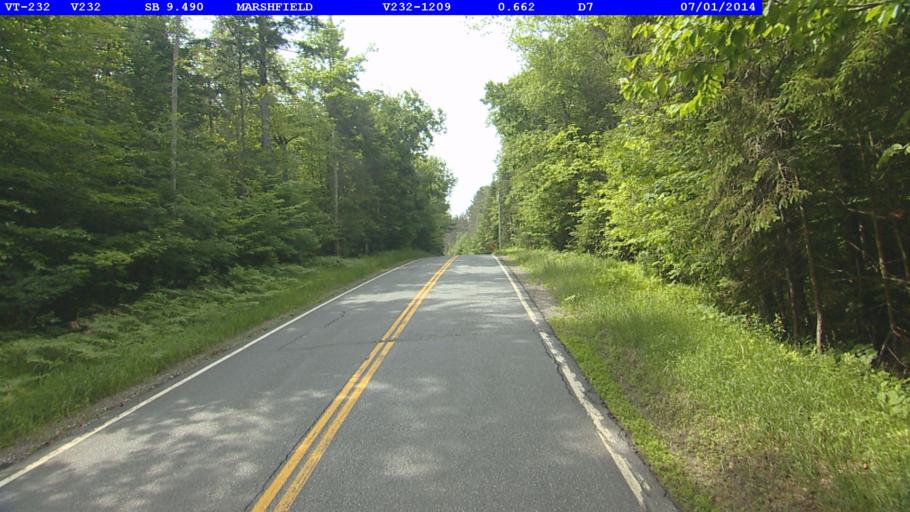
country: US
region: Vermont
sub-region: Caledonia County
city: Hardwick
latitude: 44.3255
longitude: -72.2893
